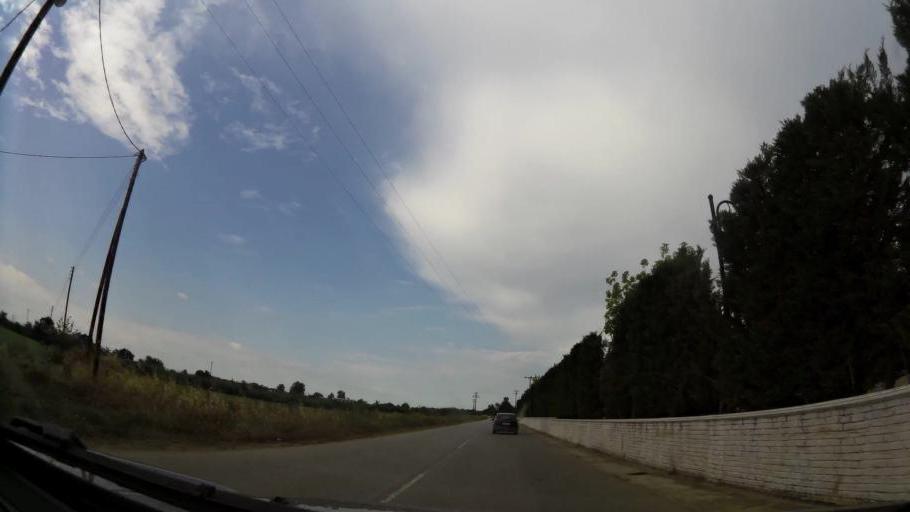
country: GR
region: Central Macedonia
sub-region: Nomos Pierias
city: Paralia
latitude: 40.2872
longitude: 22.6064
